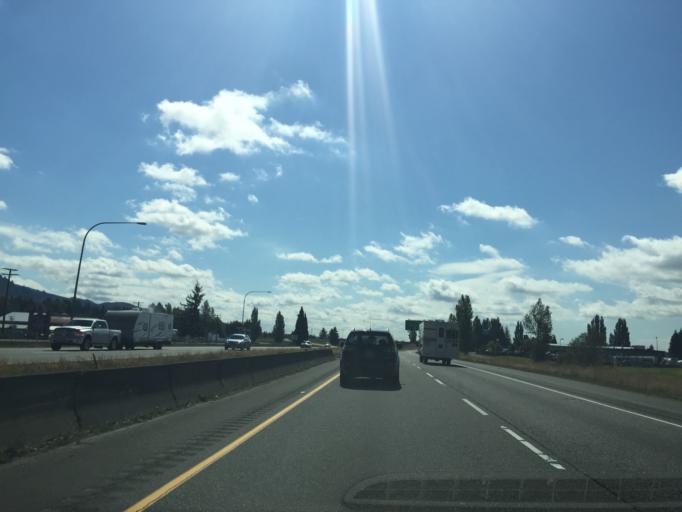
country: US
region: Washington
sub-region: Skagit County
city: Mount Vernon
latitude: 48.4049
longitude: -122.3309
